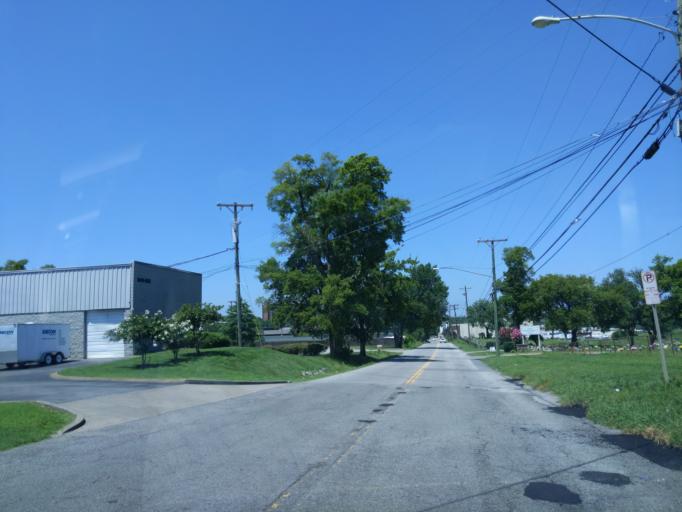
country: US
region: Tennessee
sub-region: Davidson County
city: Nashville
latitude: 36.1448
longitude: -86.7451
